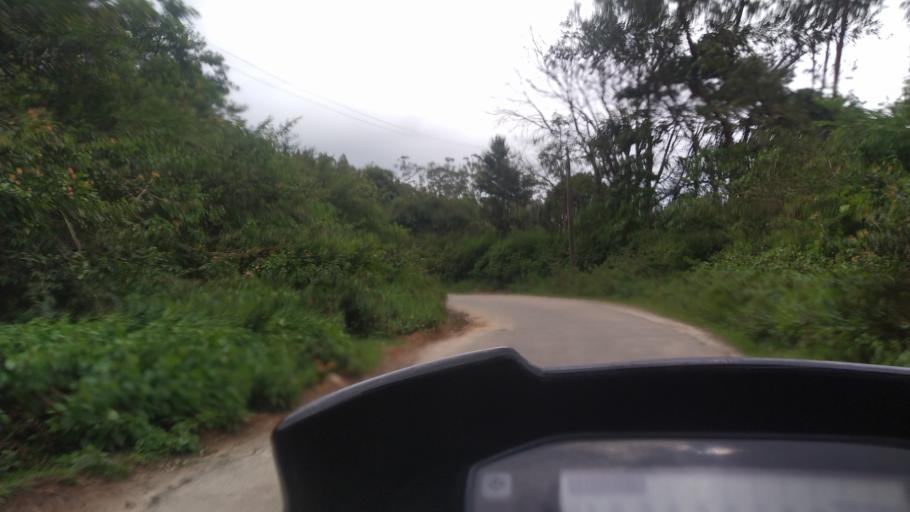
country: IN
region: Kerala
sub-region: Idukki
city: Munnar
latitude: 10.0652
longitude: 77.1014
